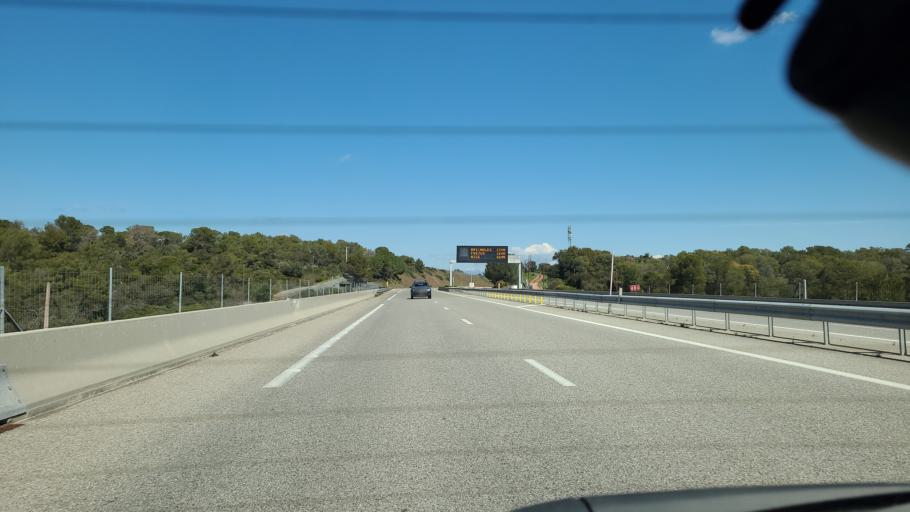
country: FR
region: Provence-Alpes-Cote d'Azur
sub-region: Departement du Var
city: Le Cannet-des-Maures
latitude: 43.3725
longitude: 6.3461
